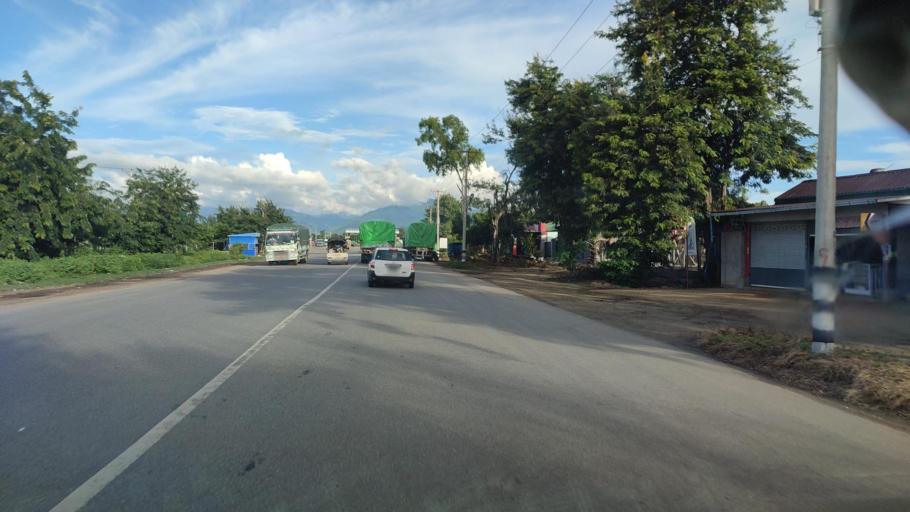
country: MM
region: Mandalay
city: Yamethin
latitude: 20.1149
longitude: 96.2224
